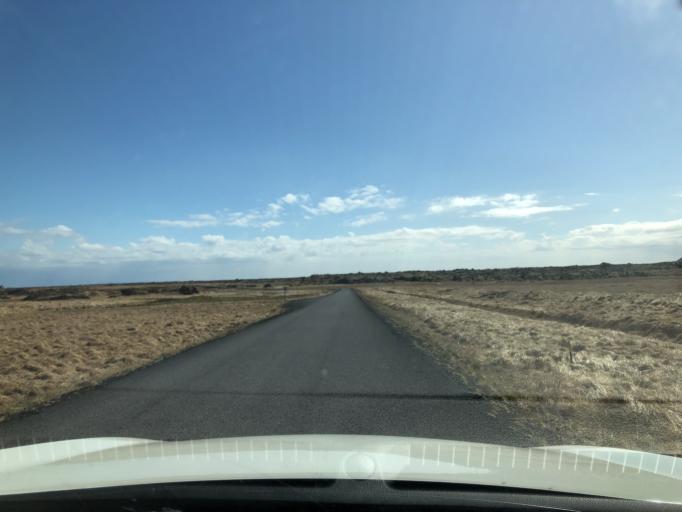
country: IS
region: West
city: Olafsvik
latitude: 64.8308
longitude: -23.4059
